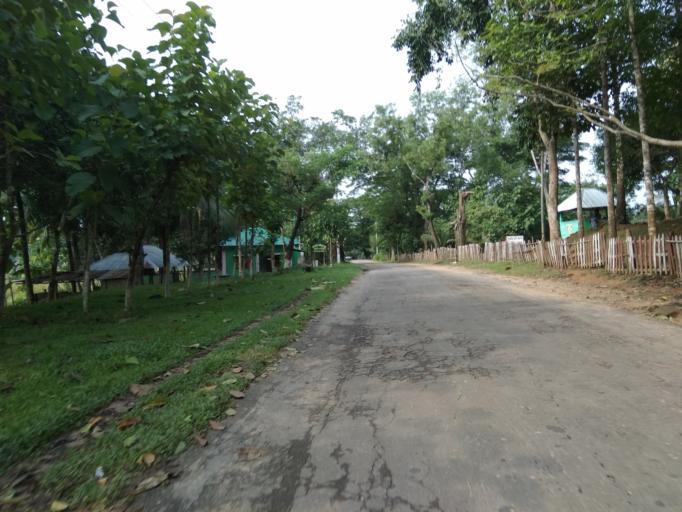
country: BD
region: Chittagong
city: Khagrachhari
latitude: 23.0200
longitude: 92.0137
